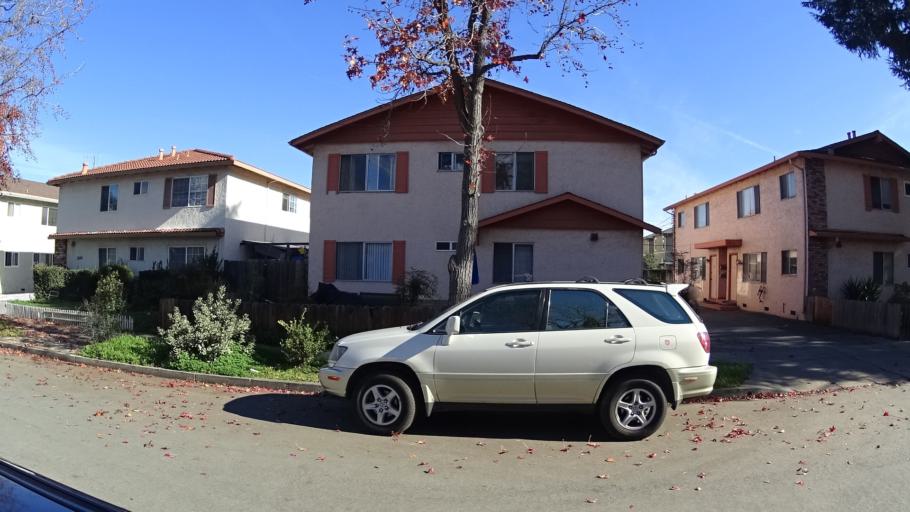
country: US
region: California
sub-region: Santa Clara County
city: Cupertino
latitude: 37.3424
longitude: -122.0386
